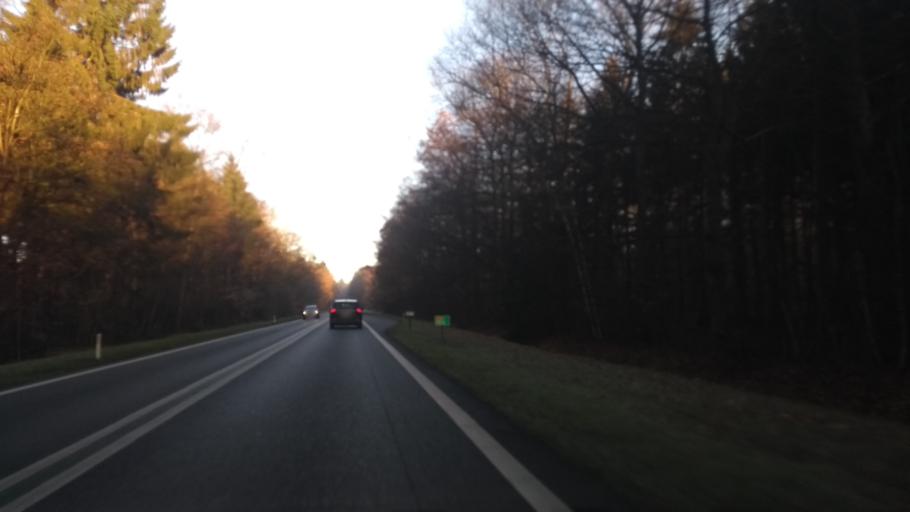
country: NL
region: Overijssel
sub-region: Gemeente Twenterand
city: Magele
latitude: 52.5393
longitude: 6.5455
